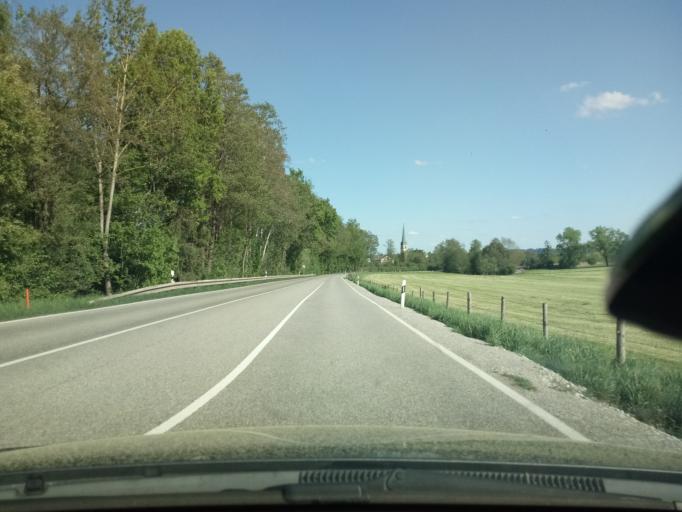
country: DE
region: Bavaria
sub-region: Upper Bavaria
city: Aschau am Inn
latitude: 48.2009
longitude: 12.3388
